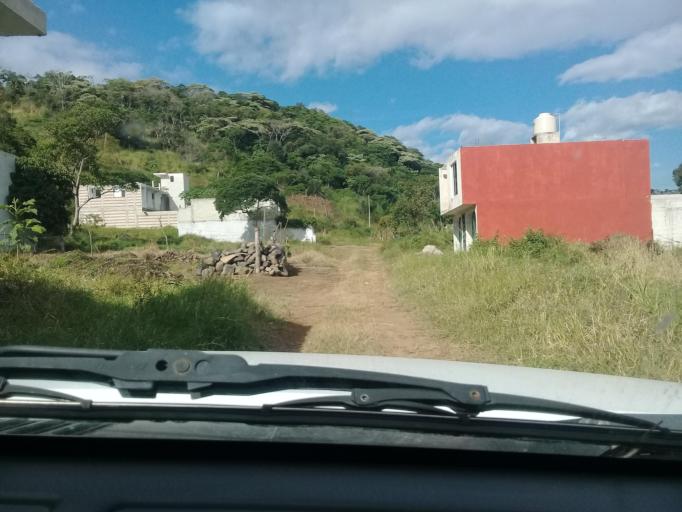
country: MX
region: Veracruz
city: El Castillo
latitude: 19.5440
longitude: -96.8792
